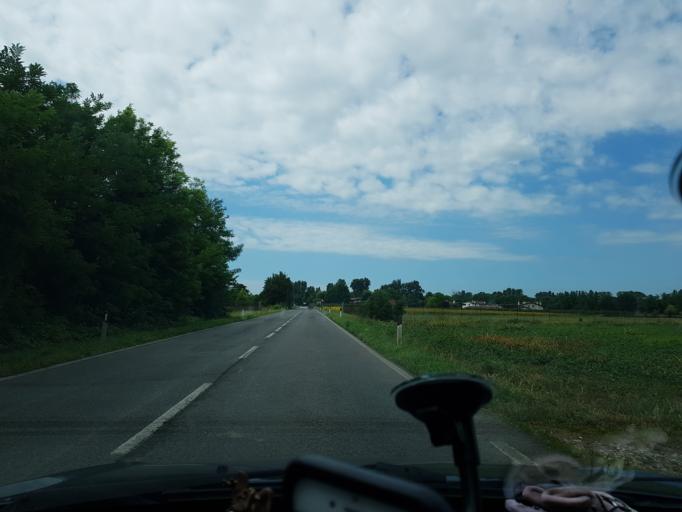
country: IT
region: Friuli Venezia Giulia
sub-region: Provincia di Gorizia
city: Turriaco
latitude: 45.8290
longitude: 13.4392
